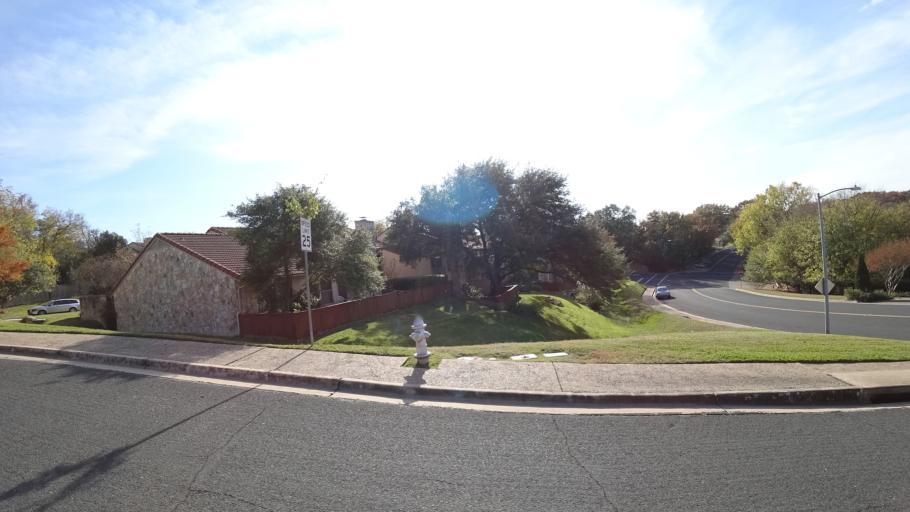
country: US
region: Texas
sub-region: Williamson County
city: Jollyville
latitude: 30.3790
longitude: -97.7574
